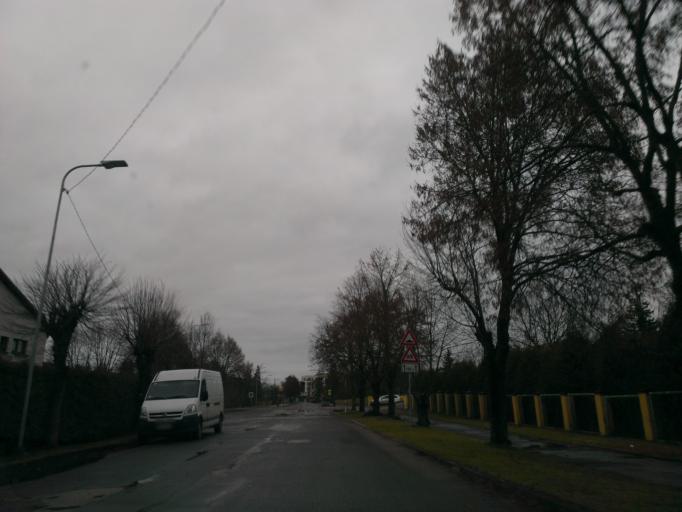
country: LV
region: Adazi
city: Adazi
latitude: 57.0738
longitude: 24.3241
